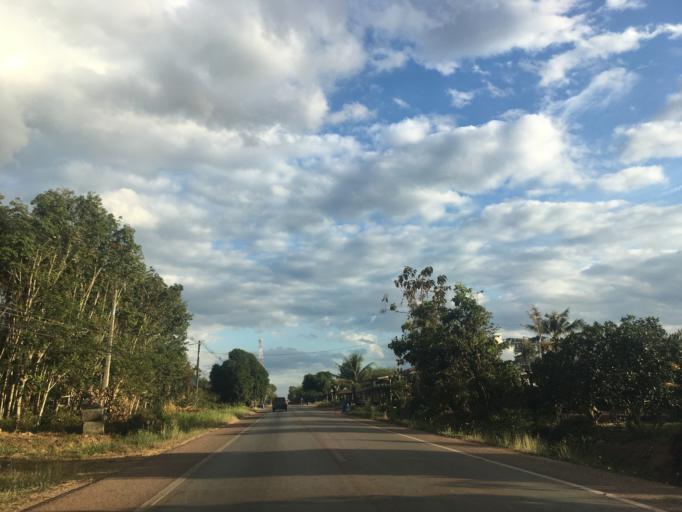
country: TH
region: Chanthaburi
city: Na Yai Am
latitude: 12.7393
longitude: 101.7397
